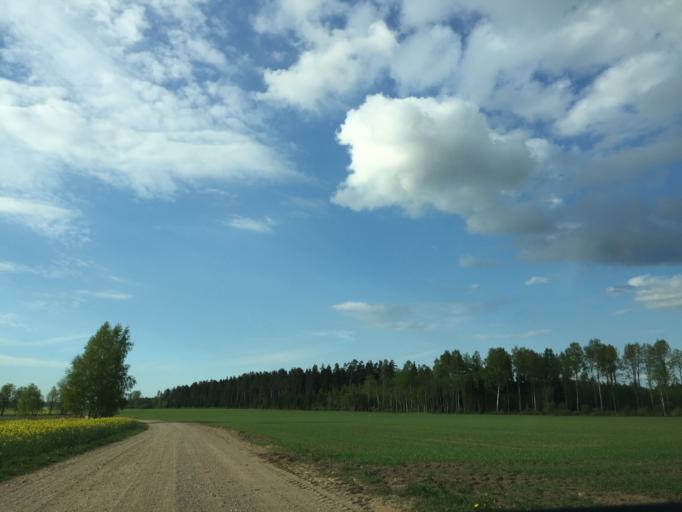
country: LV
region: Limbazu Rajons
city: Limbazi
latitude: 57.3543
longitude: 24.7006
